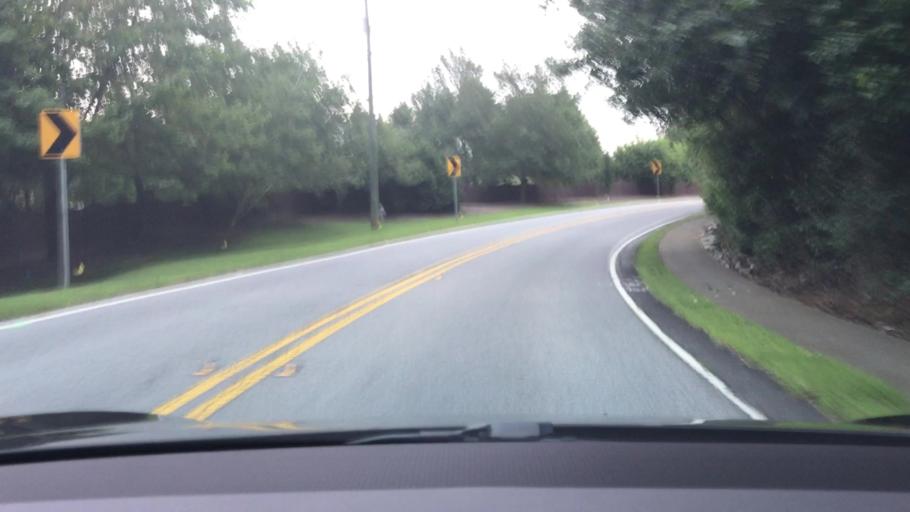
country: US
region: Georgia
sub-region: Gwinnett County
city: Suwanee
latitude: 34.0781
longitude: -84.0838
